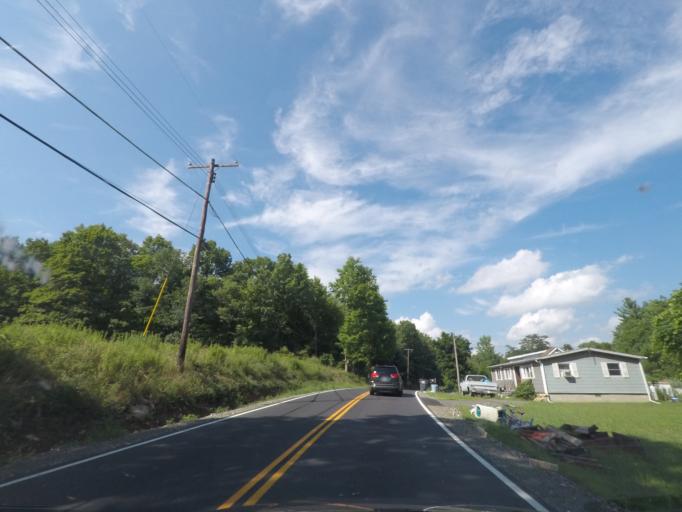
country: US
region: New York
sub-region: Rensselaer County
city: Averill Park
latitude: 42.5863
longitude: -73.5696
